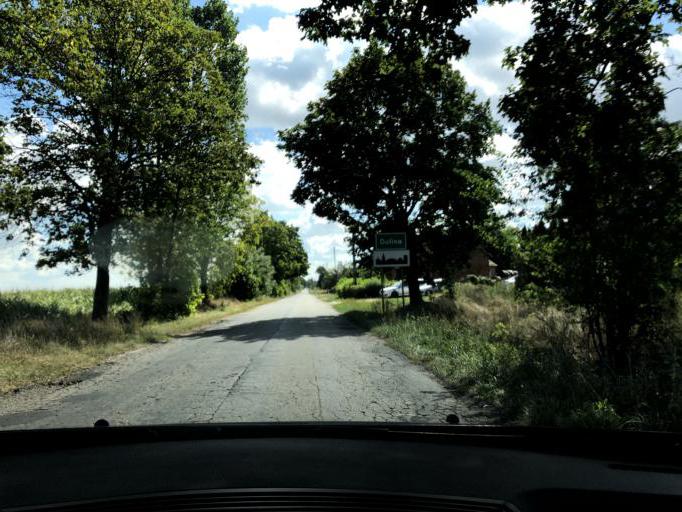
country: PL
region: Lodz Voivodeship
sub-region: Powiat wieruszowski
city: Czastary
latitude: 51.2376
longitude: 18.3406
